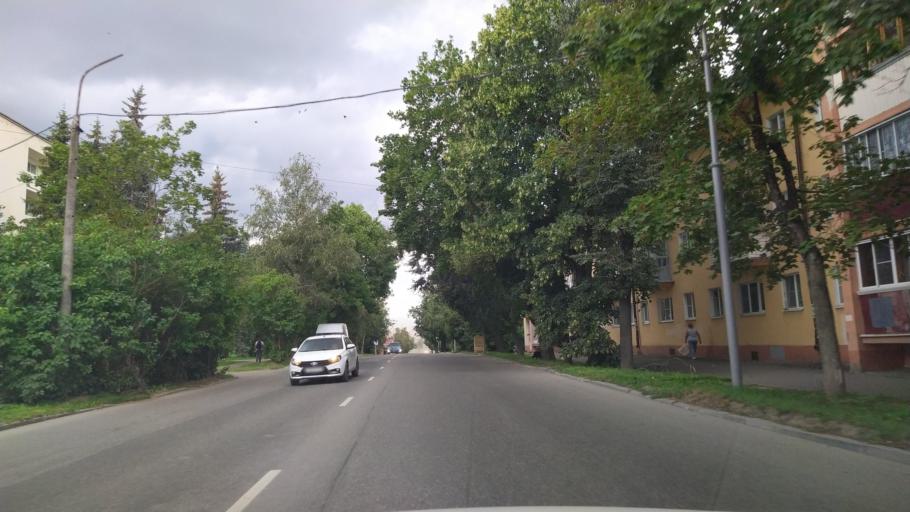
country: RU
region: Novgorod
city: Velikiy Novgorod
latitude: 58.5191
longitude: 31.2641
